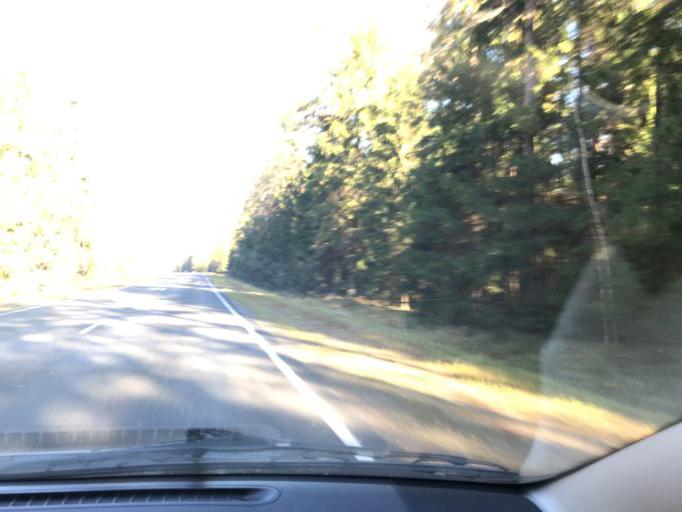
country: BY
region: Vitebsk
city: Lyepyel'
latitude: 54.9679
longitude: 28.7451
